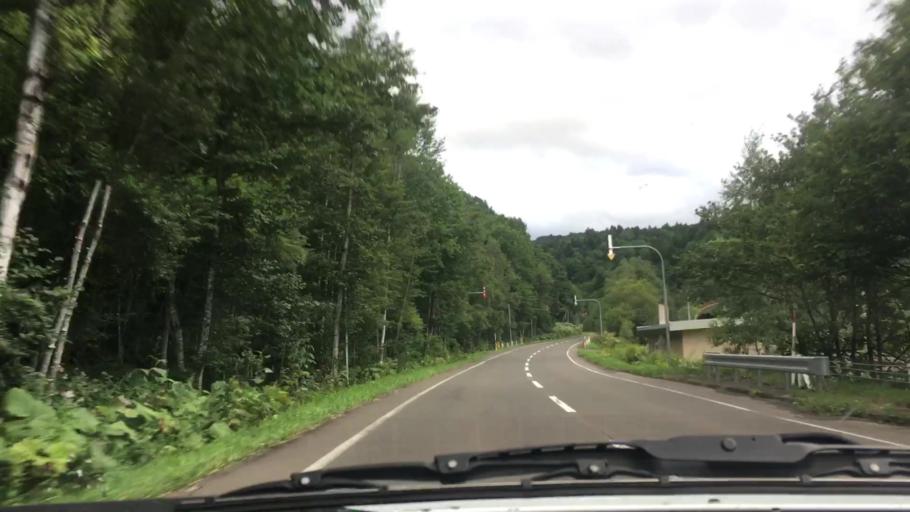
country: JP
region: Hokkaido
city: Shimo-furano
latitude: 43.0739
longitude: 142.6733
